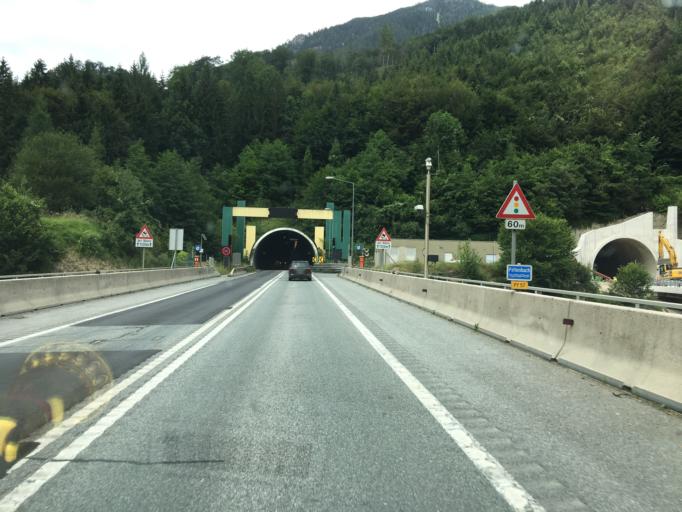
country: AT
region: Upper Austria
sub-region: Politischer Bezirk Kirchdorf an der Krems
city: Micheldorf in Oberoesterreich
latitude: 47.7858
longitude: 14.1747
